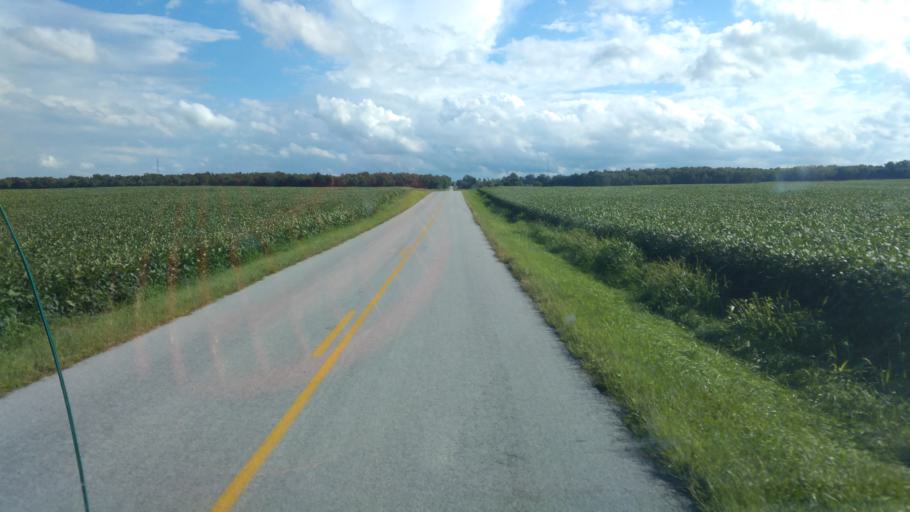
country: US
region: Ohio
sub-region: Hardin County
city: Kenton
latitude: 40.6784
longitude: -83.6337
